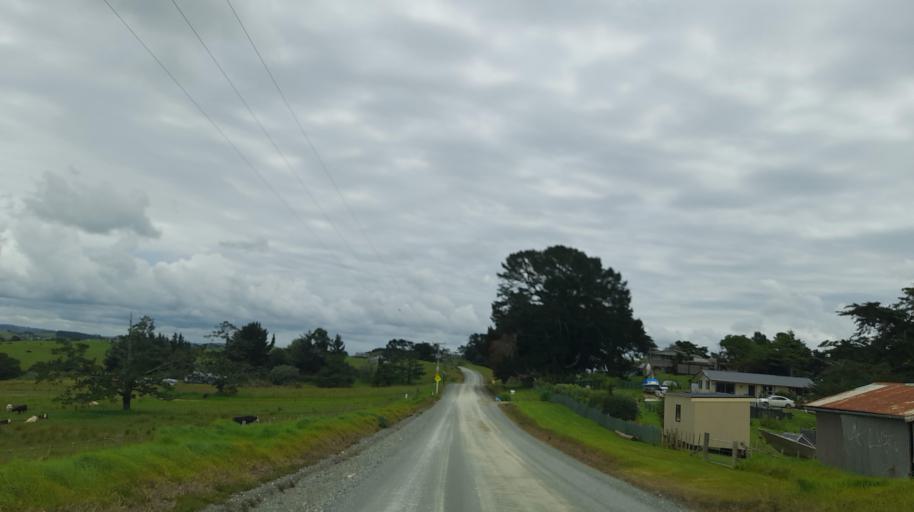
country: NZ
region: Auckland
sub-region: Auckland
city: Wellsford
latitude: -36.2495
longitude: 174.4181
